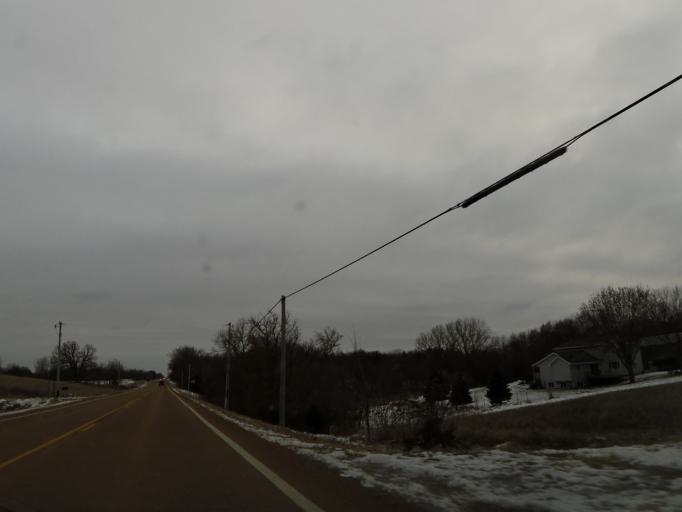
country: US
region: Minnesota
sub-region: Carver County
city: Carver
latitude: 44.7240
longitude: -93.6485
